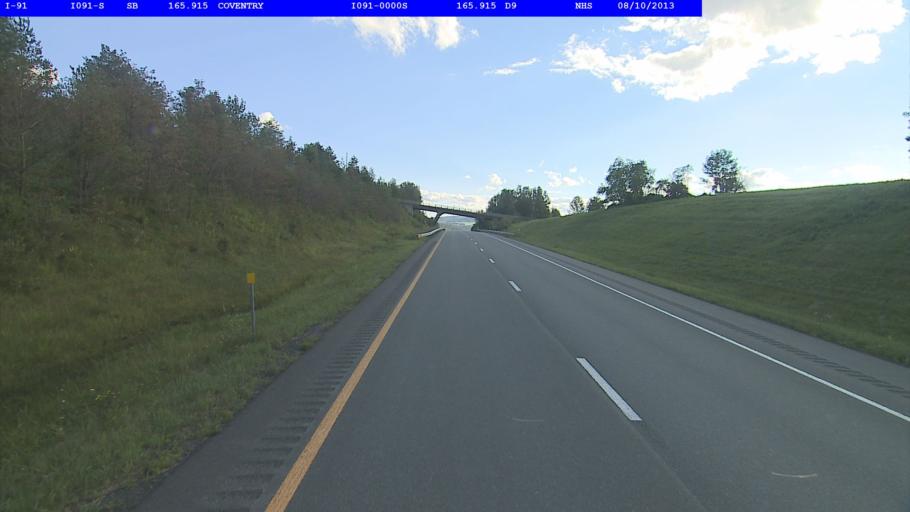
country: US
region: Vermont
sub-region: Orleans County
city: Newport
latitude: 44.8662
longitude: -72.1837
